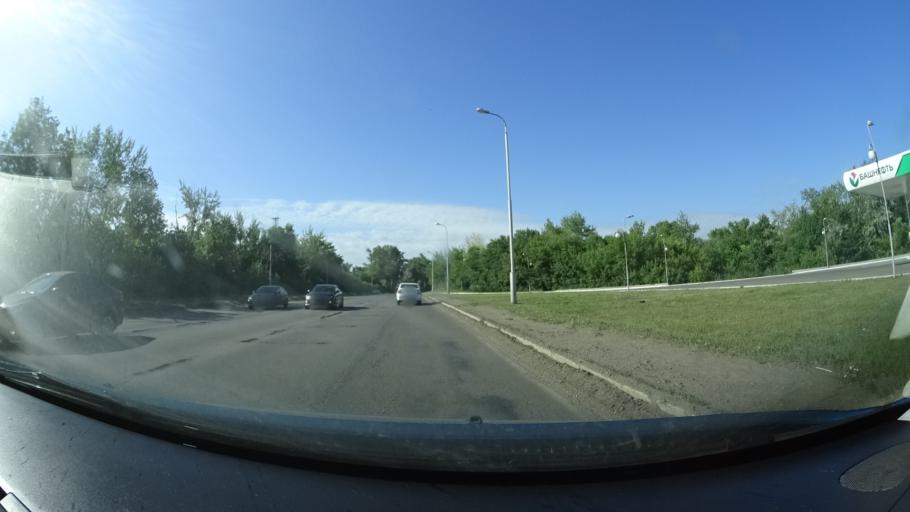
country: RU
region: Bashkortostan
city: Ufa
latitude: 54.8462
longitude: 56.0765
